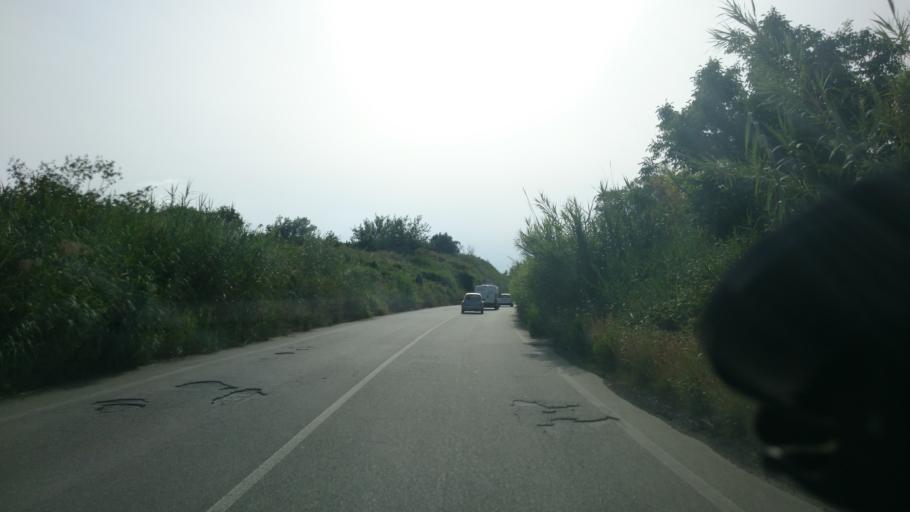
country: IT
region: Calabria
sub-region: Provincia di Vibo-Valentia
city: Stefanaconi
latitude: 38.7064
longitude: 16.1112
